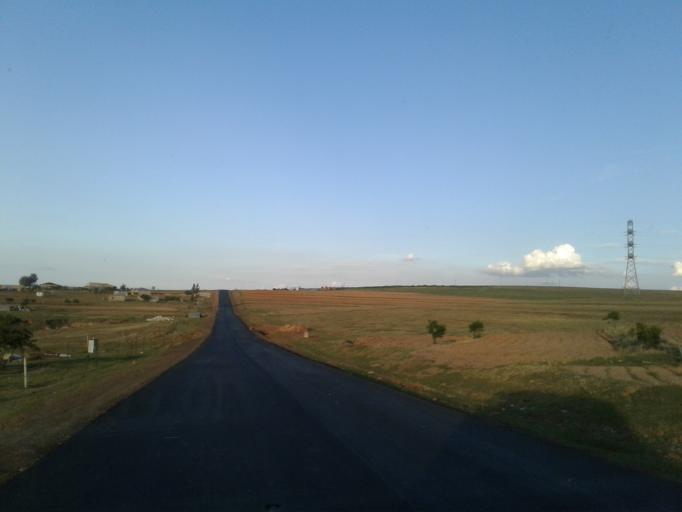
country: LS
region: Maseru
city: Maseru
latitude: -29.3134
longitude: 27.5943
